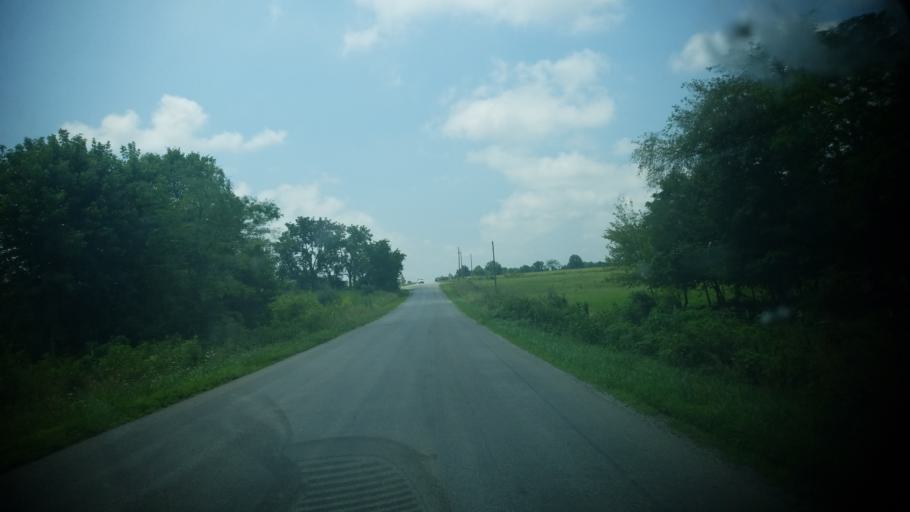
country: US
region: Illinois
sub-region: Wayne County
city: Fairfield
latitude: 38.5138
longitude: -88.3485
